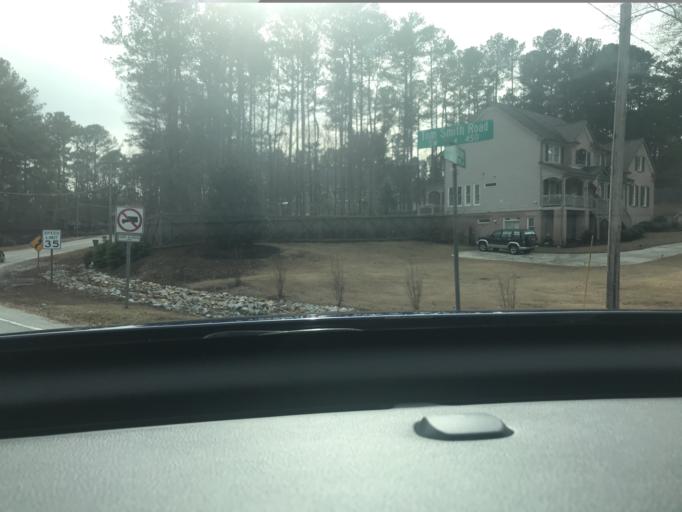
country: US
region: Georgia
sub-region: Gwinnett County
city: Lilburn
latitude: 33.8868
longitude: -84.0937
